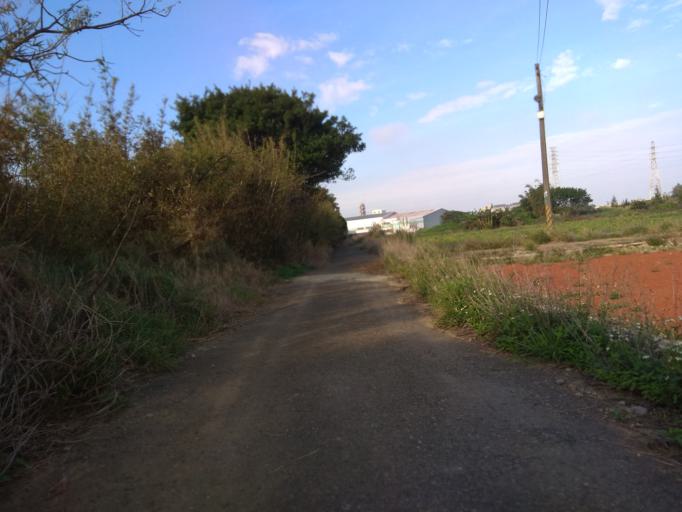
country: TW
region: Taiwan
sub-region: Hsinchu
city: Zhubei
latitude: 24.9845
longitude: 121.0382
